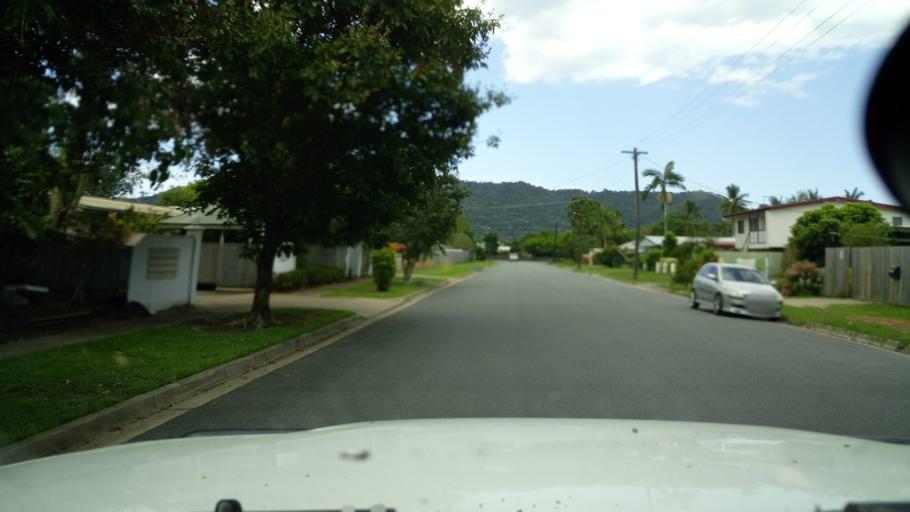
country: AU
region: Queensland
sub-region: Cairns
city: Cairns
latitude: -16.9151
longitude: 145.7365
